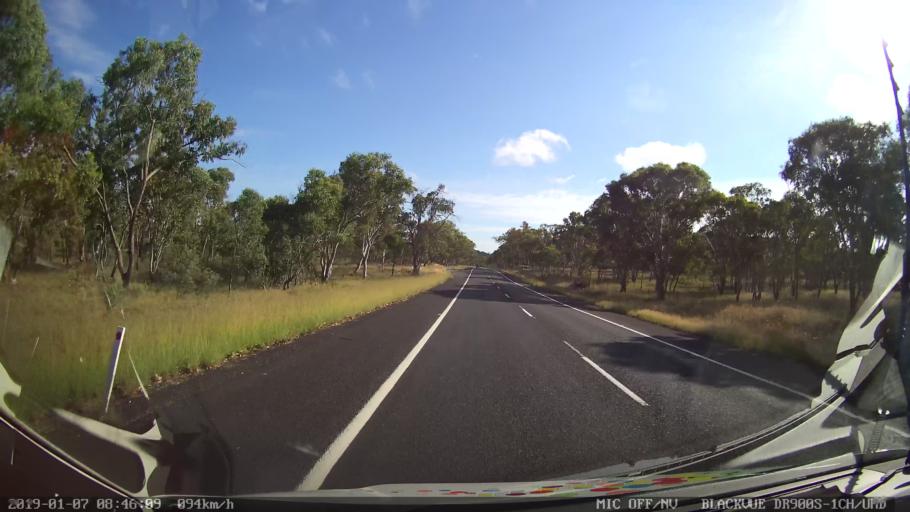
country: AU
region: New South Wales
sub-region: Tamworth Municipality
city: Kootingal
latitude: -30.8106
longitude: 151.2318
